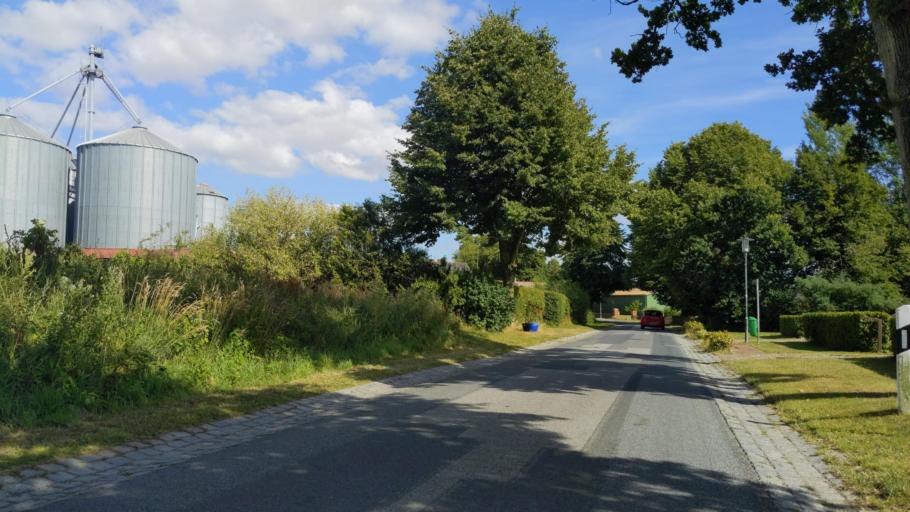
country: DE
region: Schleswig-Holstein
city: Monkhagen
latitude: 53.9491
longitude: 10.5537
